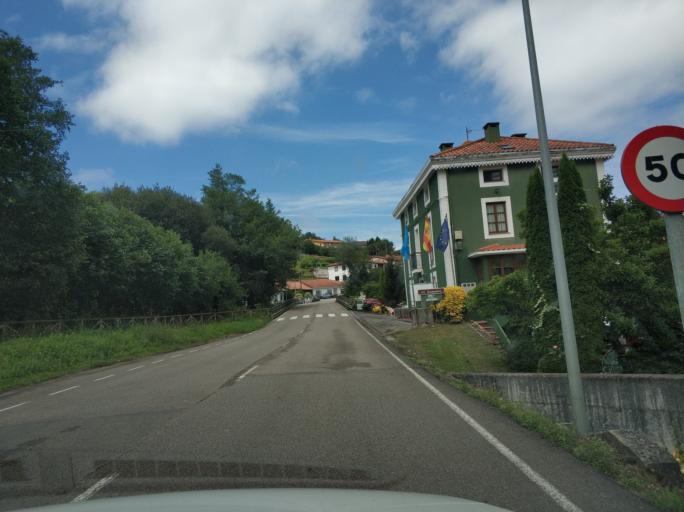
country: ES
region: Asturias
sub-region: Province of Asturias
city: Cudillero
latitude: 43.5593
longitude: -6.2294
